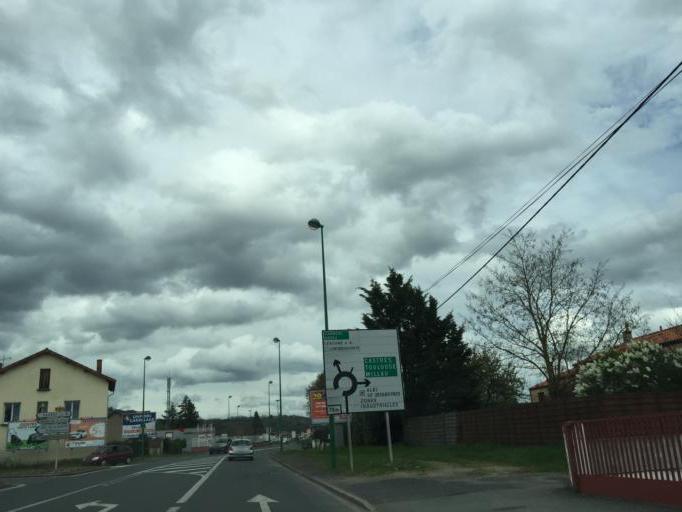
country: FR
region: Midi-Pyrenees
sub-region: Departement du Tarn
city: Albi
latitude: 43.9505
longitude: 2.1537
